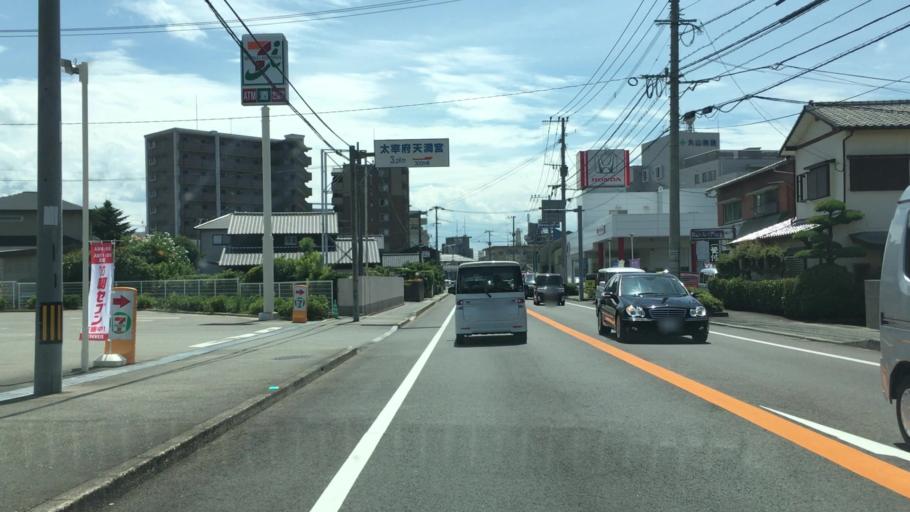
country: JP
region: Fukuoka
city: Dazaifu
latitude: 33.5152
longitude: 130.5055
